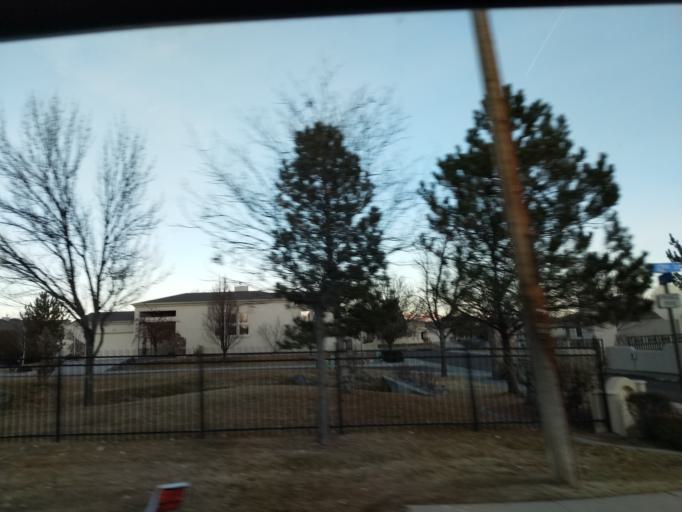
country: US
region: Colorado
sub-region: Mesa County
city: Grand Junction
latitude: 39.1052
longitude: -108.5523
